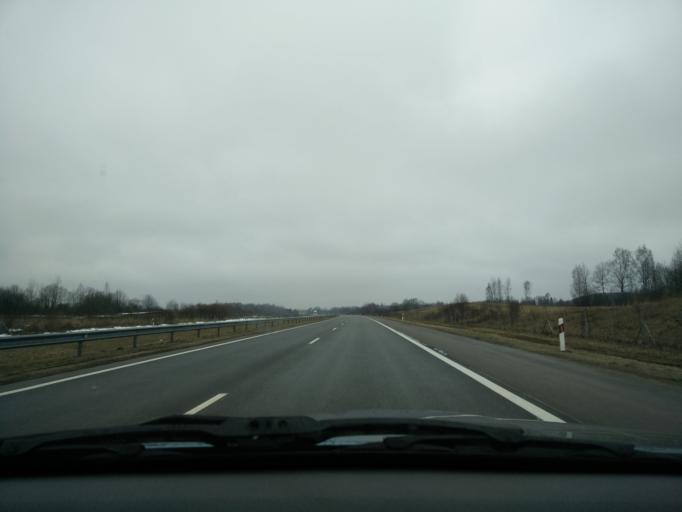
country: LT
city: Silale
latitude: 55.5471
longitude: 22.2756
